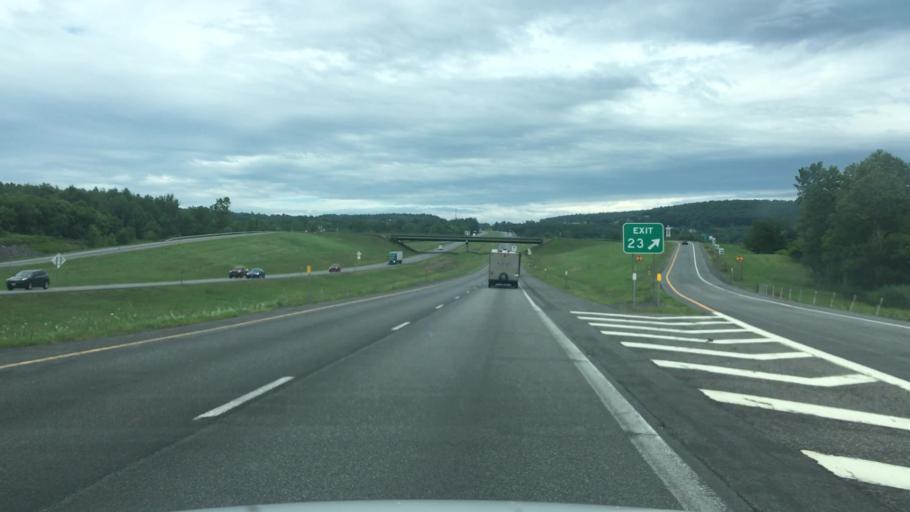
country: US
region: New York
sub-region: Schoharie County
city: Schoharie
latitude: 42.7059
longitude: -74.3195
